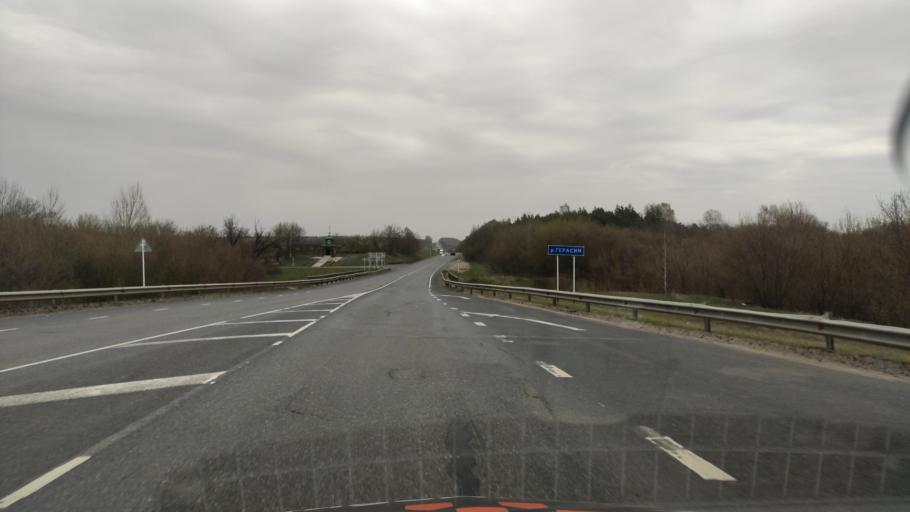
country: RU
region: Kursk
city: Gorshechnoye
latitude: 51.4687
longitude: 37.9339
